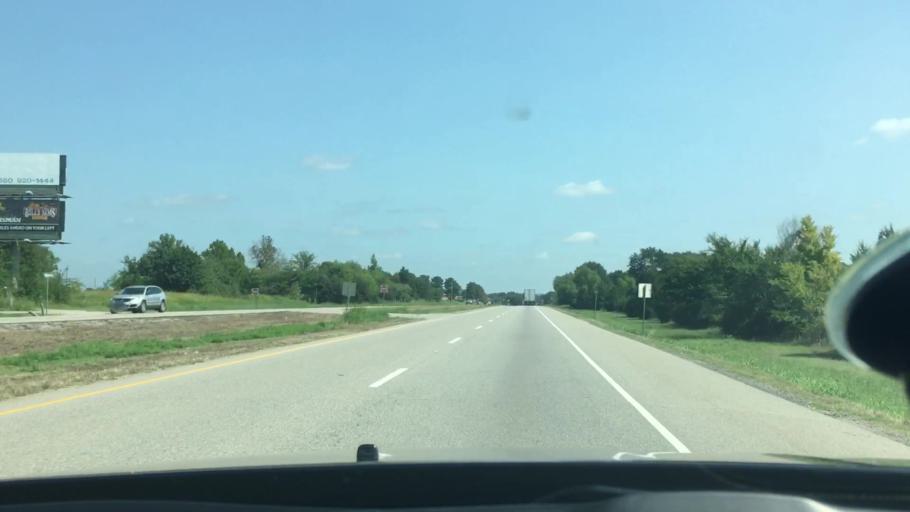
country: US
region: Oklahoma
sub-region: Atoka County
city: Atoka
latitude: 34.3485
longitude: -96.1499
